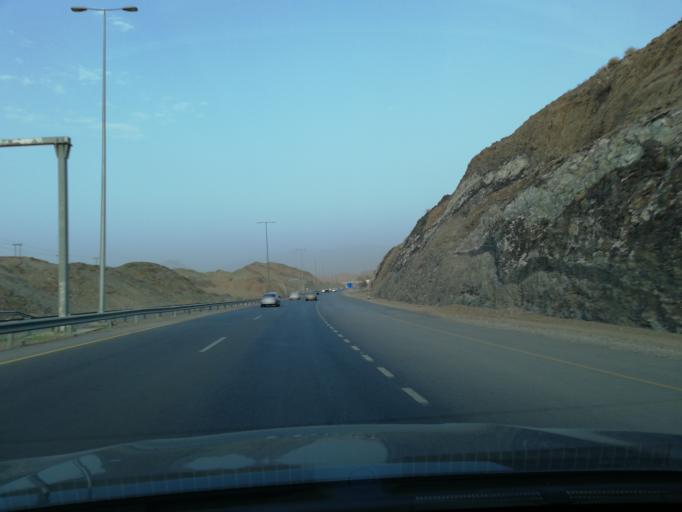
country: OM
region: Muhafazat ad Dakhiliyah
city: Bidbid
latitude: 23.4144
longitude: 58.0936
